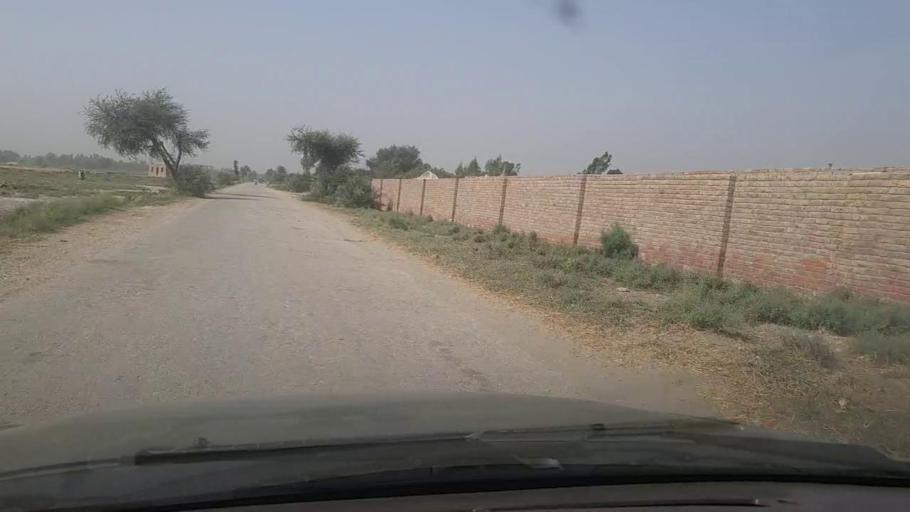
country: PK
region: Sindh
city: Shikarpur
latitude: 27.9206
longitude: 68.6112
